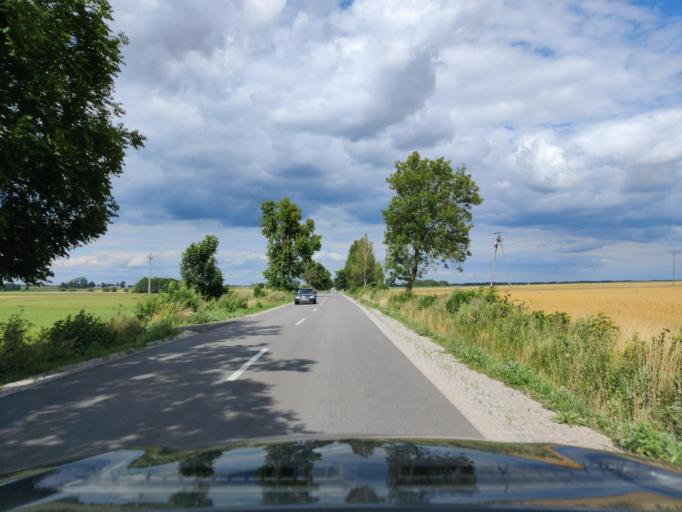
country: PL
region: Masovian Voivodeship
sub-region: Powiat sokolowski
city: Kosow Lacki
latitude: 52.5677
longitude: 22.1233
